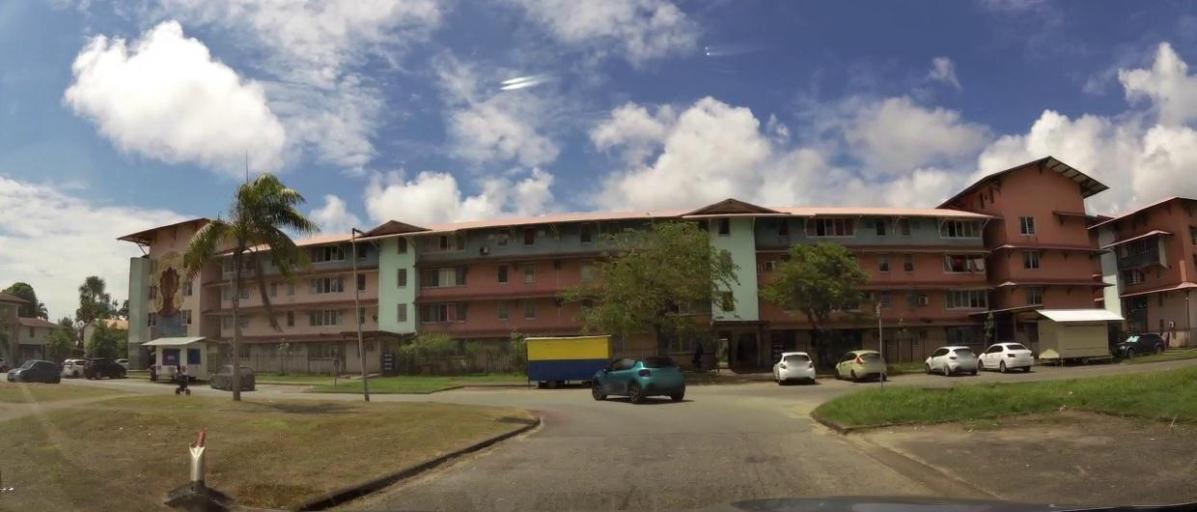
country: GF
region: Guyane
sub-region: Guyane
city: Kourou
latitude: 5.1652
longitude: -52.6523
